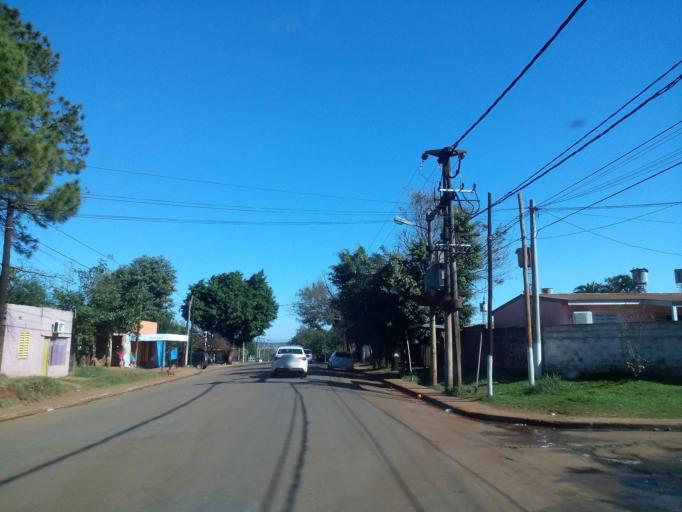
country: AR
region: Misiones
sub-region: Departamento de Capital
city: Posadas
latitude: -27.3872
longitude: -55.9362
